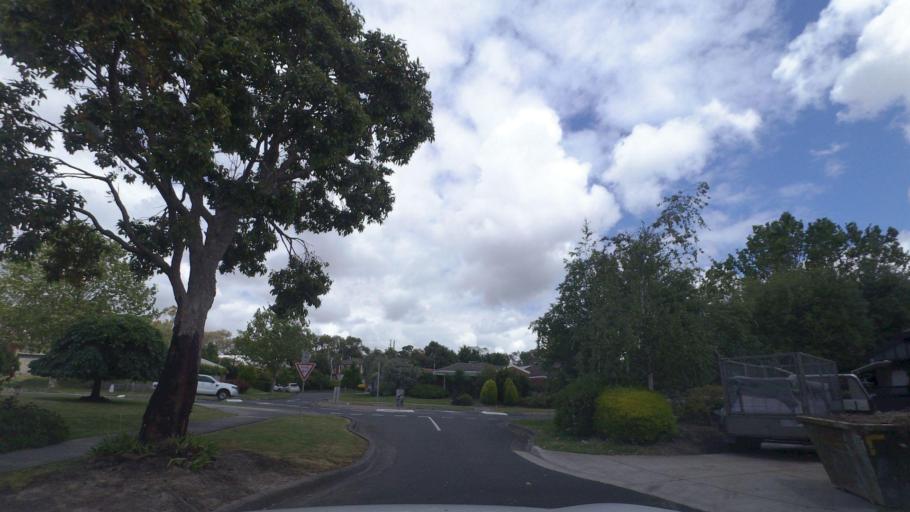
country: AU
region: Victoria
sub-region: Knox
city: Ferntree Gully
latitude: -37.9055
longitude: 145.2789
